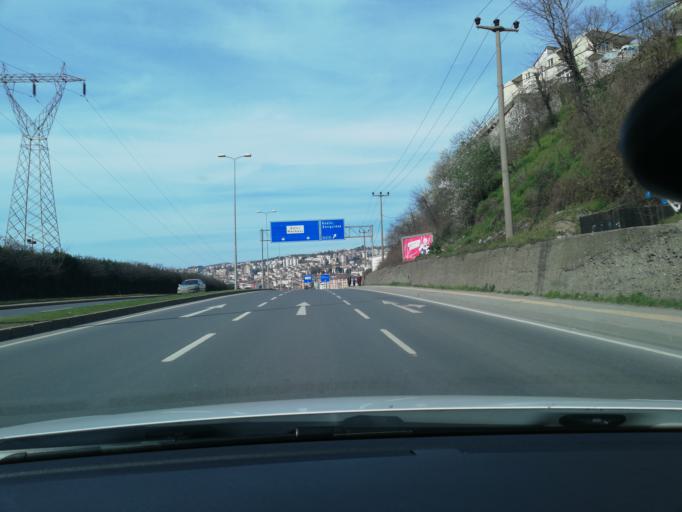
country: TR
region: Zonguldak
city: Eregli
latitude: 41.2641
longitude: 31.4353
